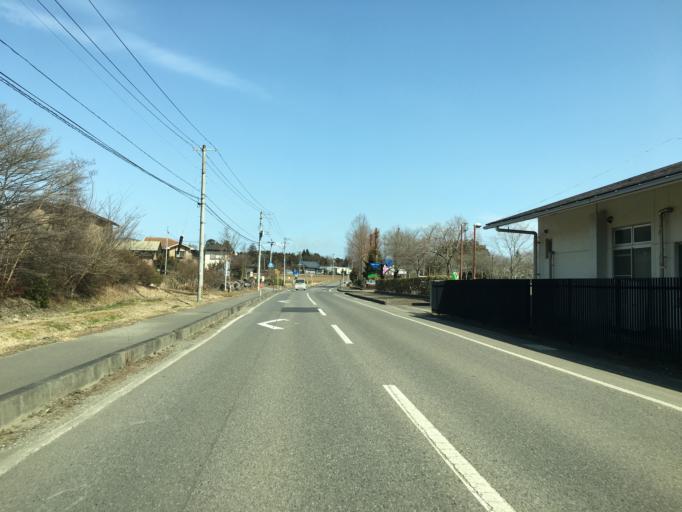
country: JP
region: Fukushima
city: Ishikawa
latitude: 37.1471
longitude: 140.3531
